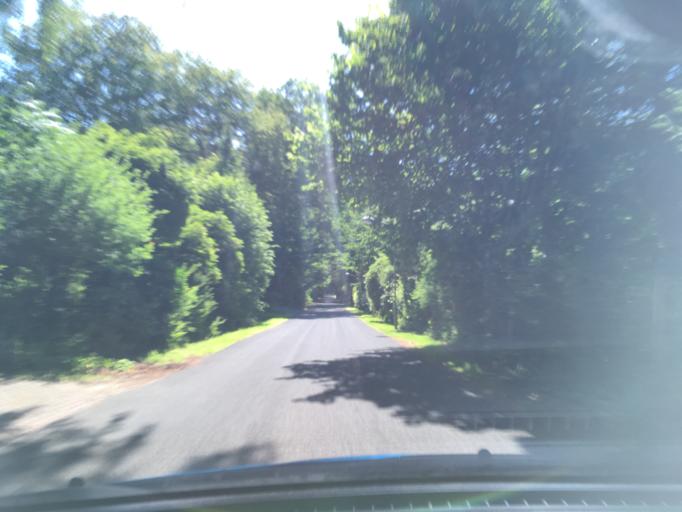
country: DE
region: Lower Saxony
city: Bendestorf
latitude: 53.3736
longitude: 9.9596
